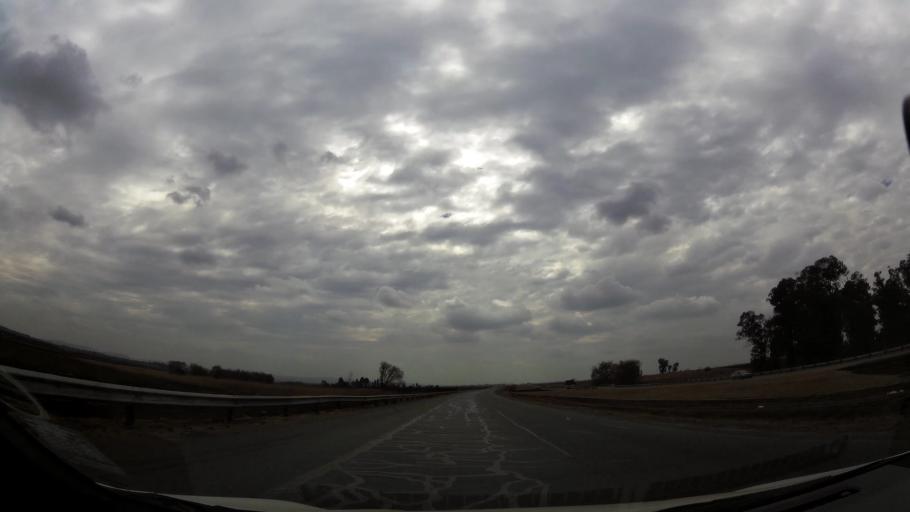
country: ZA
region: Gauteng
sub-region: Sedibeng District Municipality
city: Meyerton
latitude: -26.4032
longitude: 28.0795
